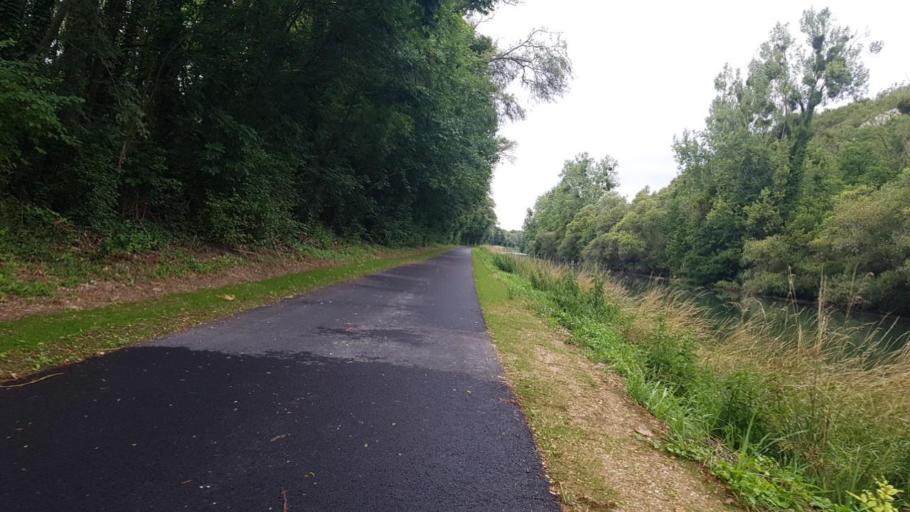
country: FR
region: Champagne-Ardenne
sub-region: Departement de la Marne
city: Vitry-le-Francois
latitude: 48.7722
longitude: 4.5501
